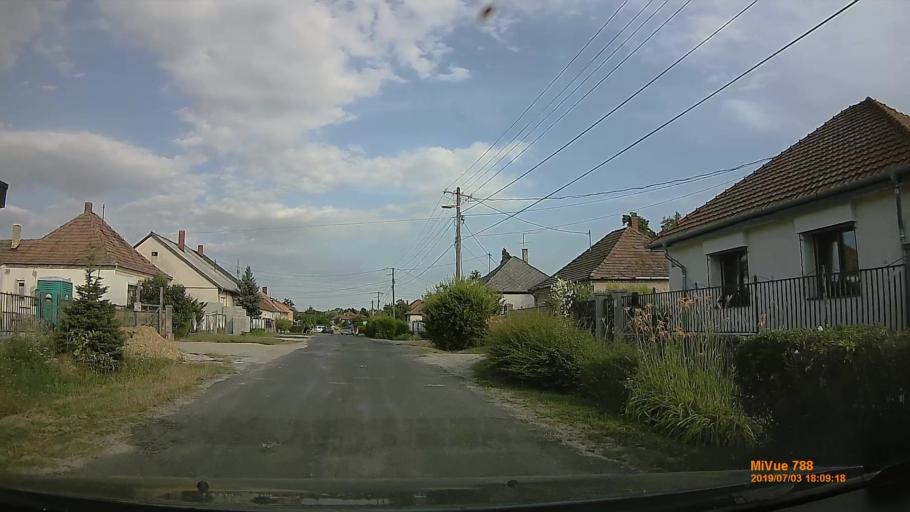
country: HU
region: Gyor-Moson-Sopron
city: Gyorujbarat
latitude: 47.6362
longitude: 17.5973
